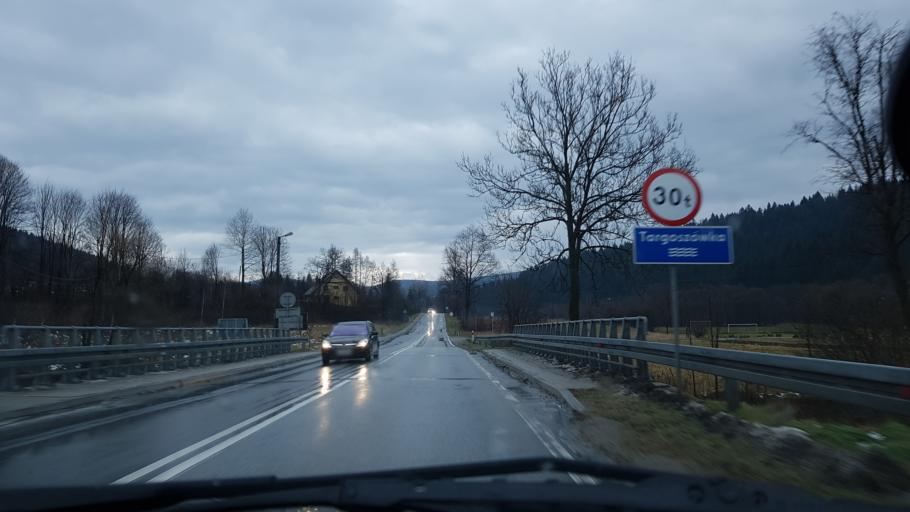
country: PL
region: Lesser Poland Voivodeship
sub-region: Powiat suski
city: Kukow
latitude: 49.7401
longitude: 19.4623
